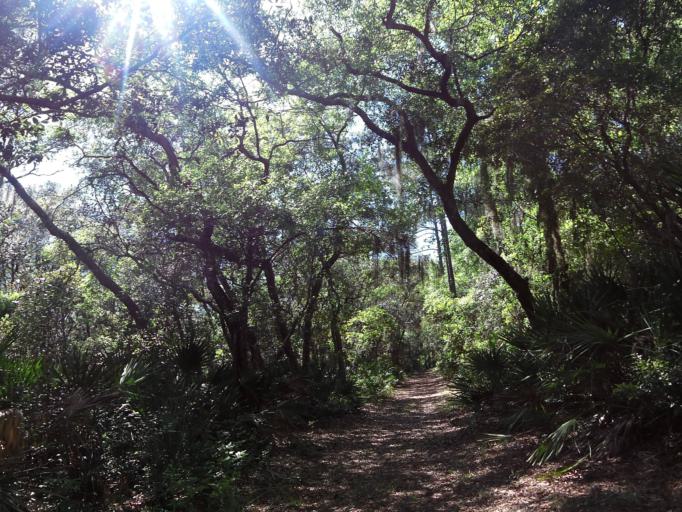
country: US
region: Florida
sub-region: Duval County
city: Atlantic Beach
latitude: 30.4506
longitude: -81.4814
